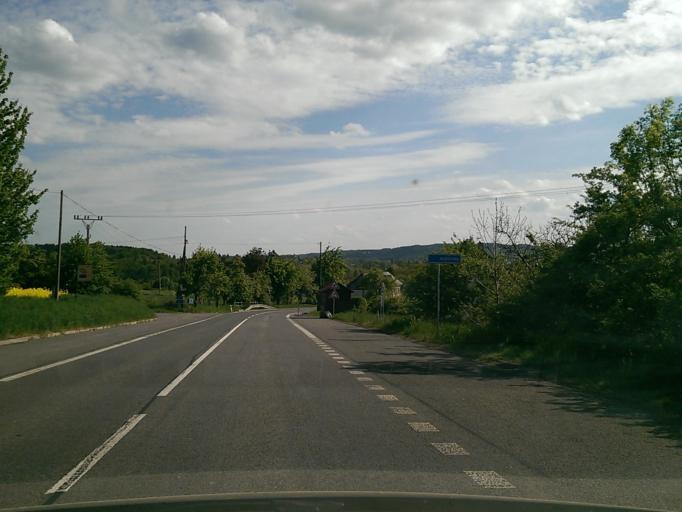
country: CZ
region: Liberecky
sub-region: Okres Semily
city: Turnov
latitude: 50.6091
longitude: 15.1646
